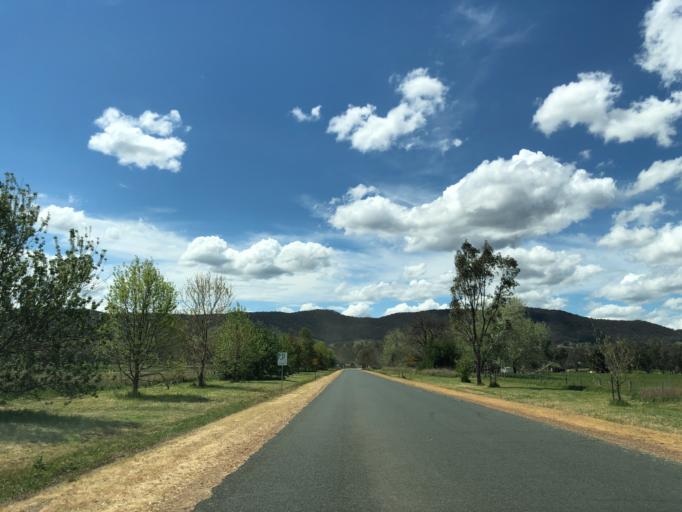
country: AU
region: Victoria
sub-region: Benalla
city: Benalla
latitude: -36.7343
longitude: 146.1023
